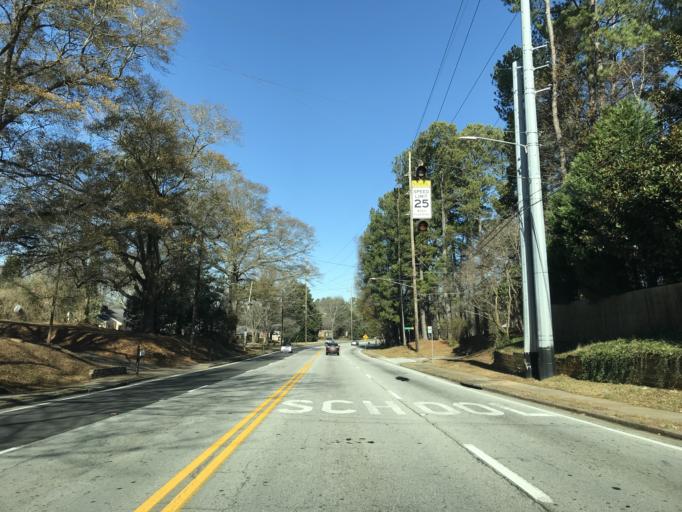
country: US
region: Georgia
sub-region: DeKalb County
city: Tucker
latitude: 33.8657
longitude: -84.2180
